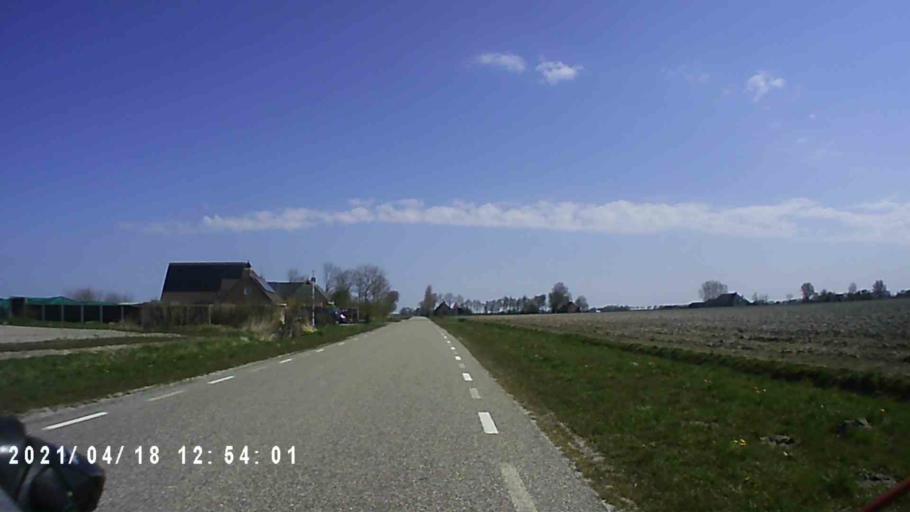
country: NL
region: Friesland
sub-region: Gemeente Dongeradeel
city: Anjum
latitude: 53.3846
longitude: 6.0687
